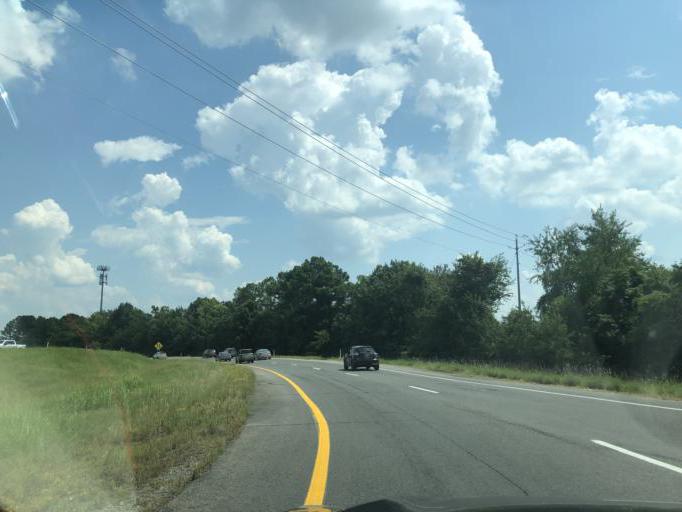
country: US
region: Tennessee
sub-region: Rutherford County
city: Murfreesboro
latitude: 35.8470
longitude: -86.4377
